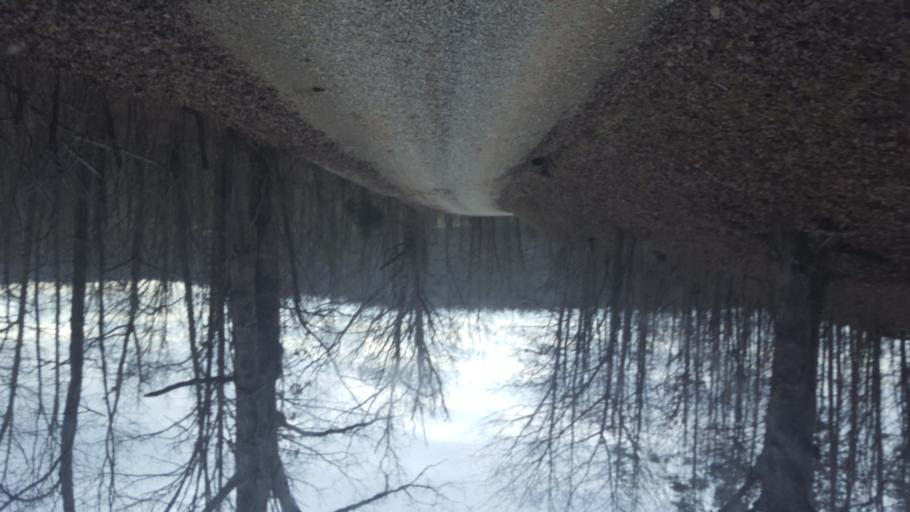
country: US
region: Ohio
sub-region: Gallia County
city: Gallipolis
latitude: 38.7338
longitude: -82.3197
